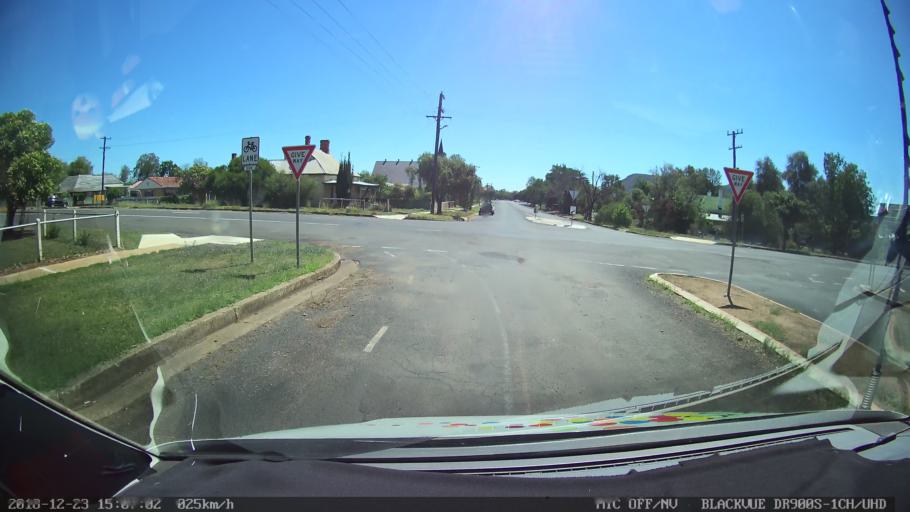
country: AU
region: New South Wales
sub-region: Tamworth Municipality
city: Manilla
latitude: -30.7464
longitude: 150.7244
